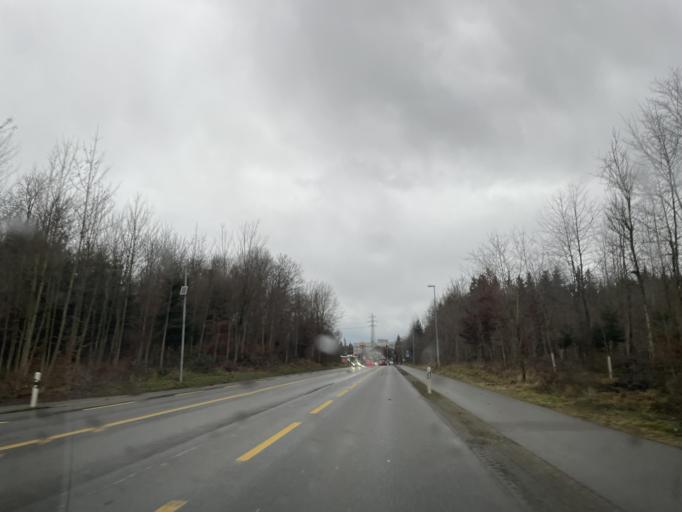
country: CH
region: Bern
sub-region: Bern-Mittelland District
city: Zollikofen
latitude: 47.0070
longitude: 7.4616
